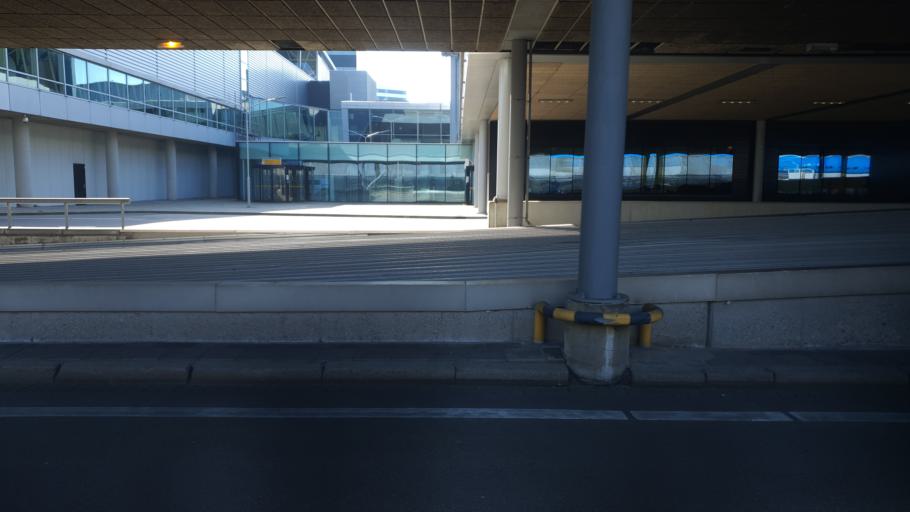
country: NL
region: North Holland
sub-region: Gemeente Aalsmeer
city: Aalsmeer
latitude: 52.3116
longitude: 4.7591
